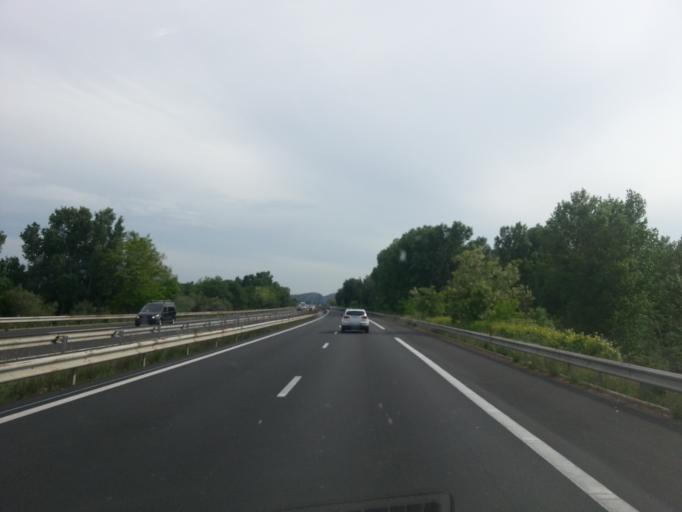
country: FR
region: Languedoc-Roussillon
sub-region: Departement du Gard
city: Montfaucon
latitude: 44.0801
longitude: 4.7723
